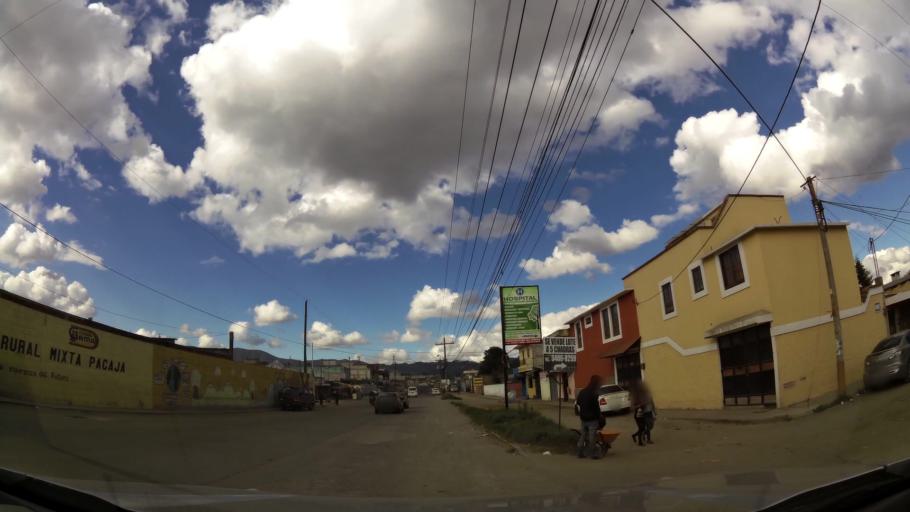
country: GT
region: Quetzaltenango
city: Quetzaltenango
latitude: 14.8357
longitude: -91.5358
